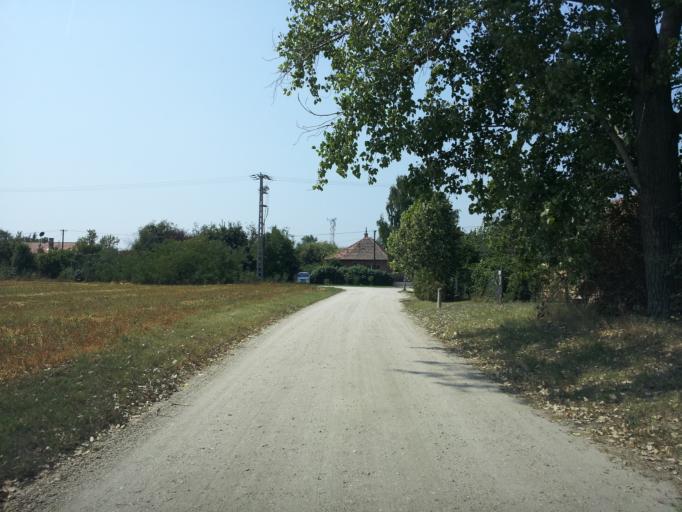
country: HU
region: Pest
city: Dunavarsany
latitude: 47.2682
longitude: 19.0734
